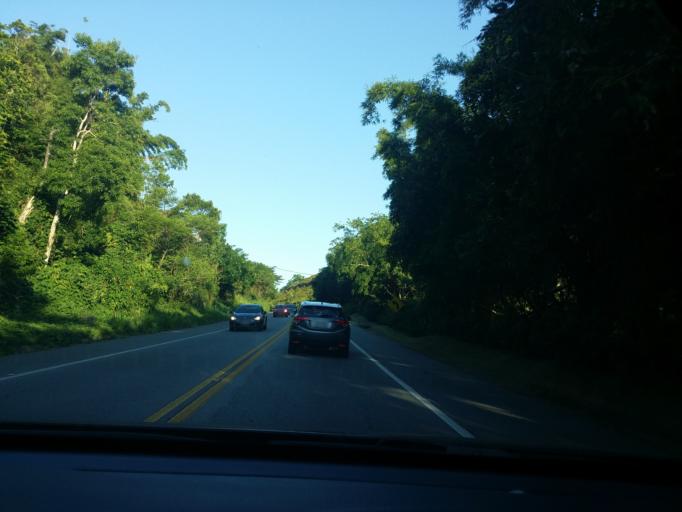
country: BR
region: Sao Paulo
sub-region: Sao Sebastiao
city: Sao Sebastiao
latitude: -23.7706
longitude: -45.7059
